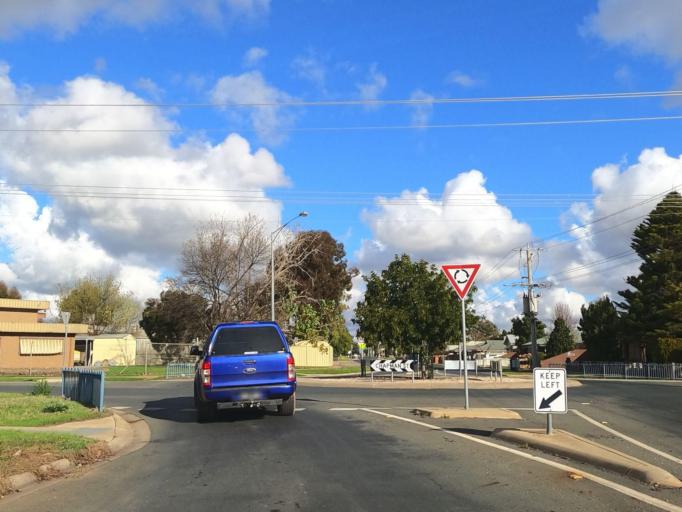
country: AU
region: Victoria
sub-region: Swan Hill
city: Swan Hill
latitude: -35.3328
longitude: 143.5524
